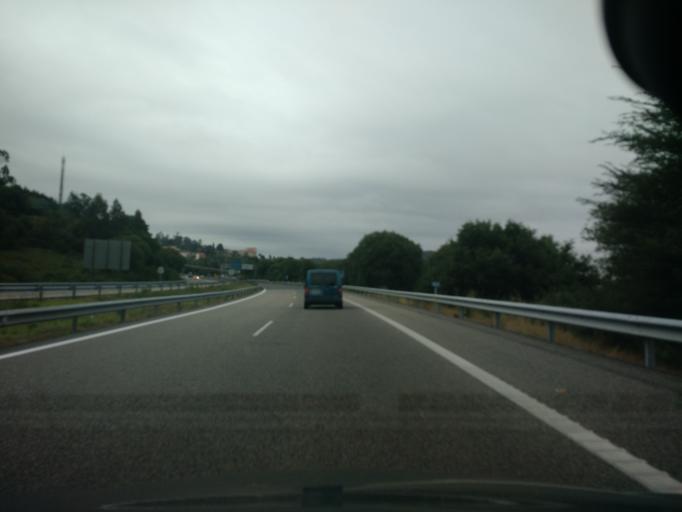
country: ES
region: Galicia
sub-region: Provincia da Coruna
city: Santiago de Compostela
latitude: 42.8962
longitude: -8.5039
